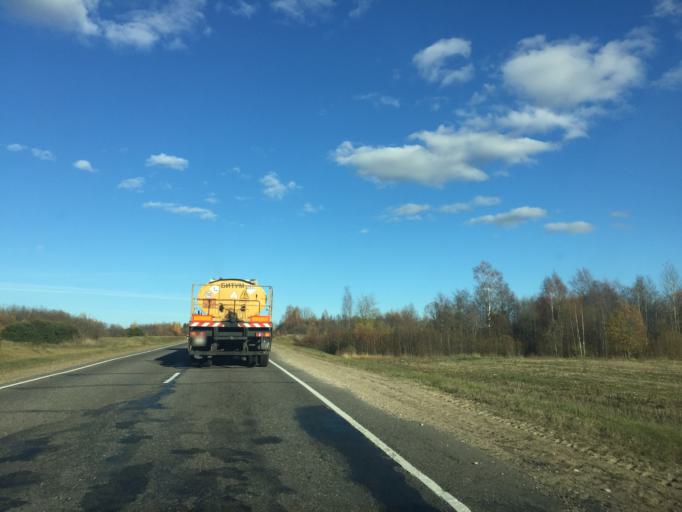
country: BY
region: Vitebsk
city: Dzisna
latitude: 55.2761
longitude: 28.1586
